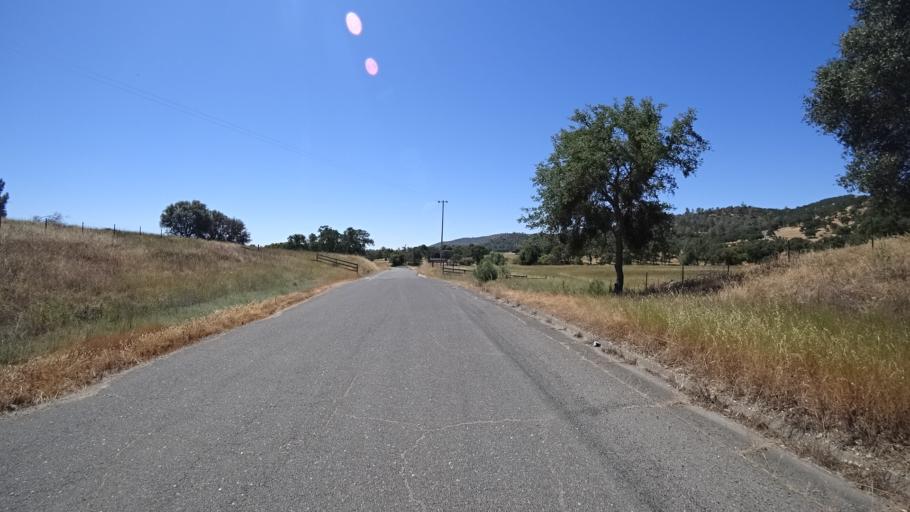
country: US
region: California
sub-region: Calaveras County
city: Copperopolis
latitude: 37.9539
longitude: -120.6864
